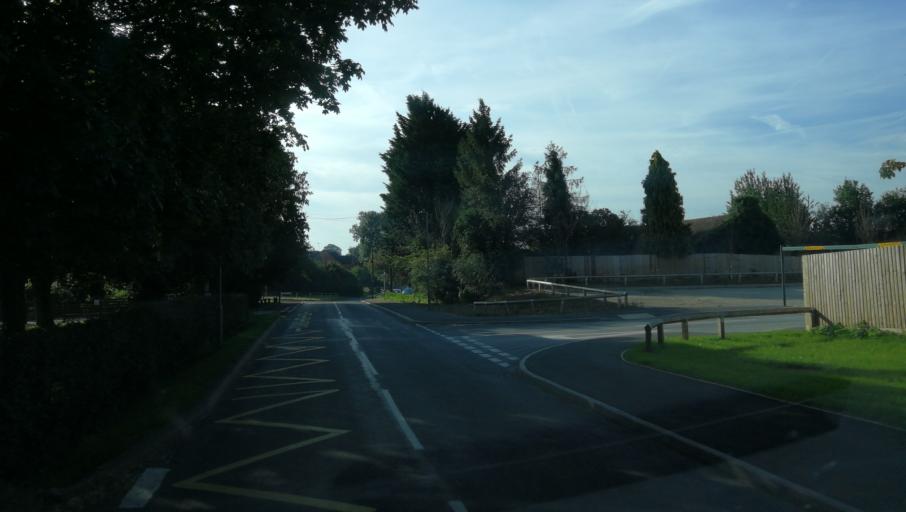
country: GB
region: England
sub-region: Oxfordshire
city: Bloxham
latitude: 52.0200
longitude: -1.3848
